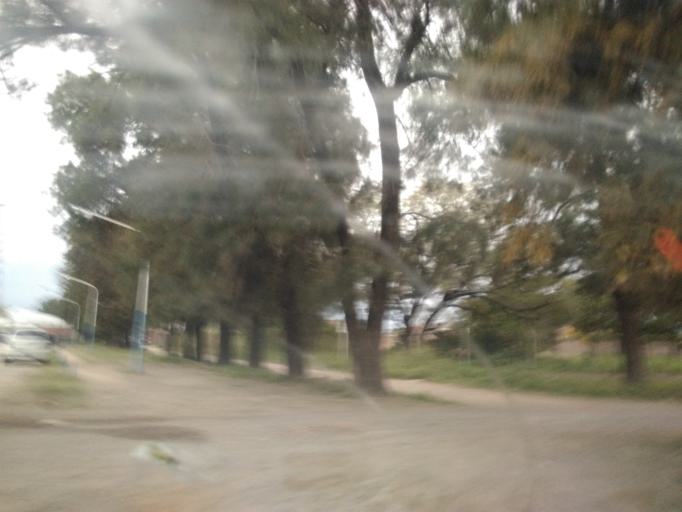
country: AR
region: Chaco
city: Fontana
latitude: -27.4418
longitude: -59.0259
